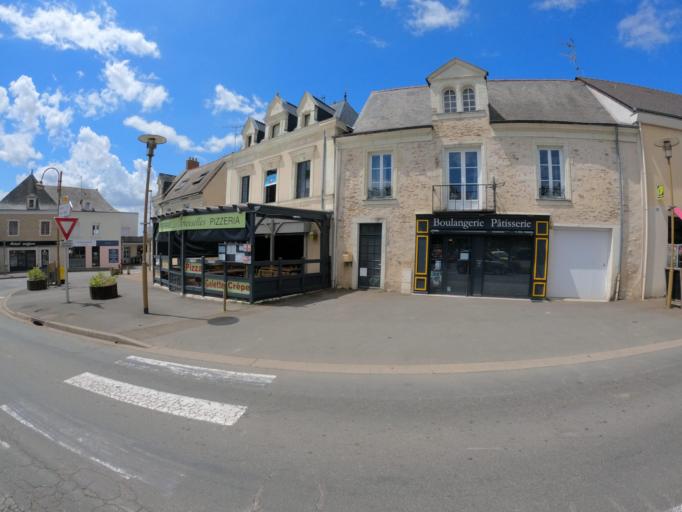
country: FR
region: Pays de la Loire
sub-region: Departement de Maine-et-Loire
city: Champigne
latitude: 47.6639
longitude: -0.5718
